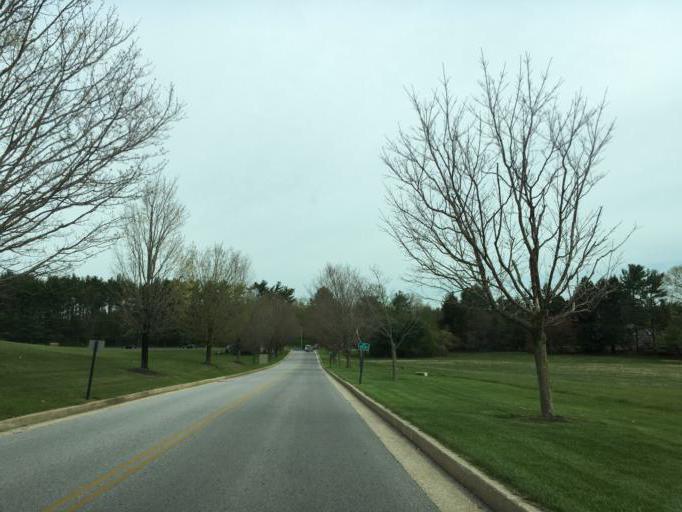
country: US
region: Maryland
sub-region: Baltimore County
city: Timonium
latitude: 39.4512
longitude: -76.5951
